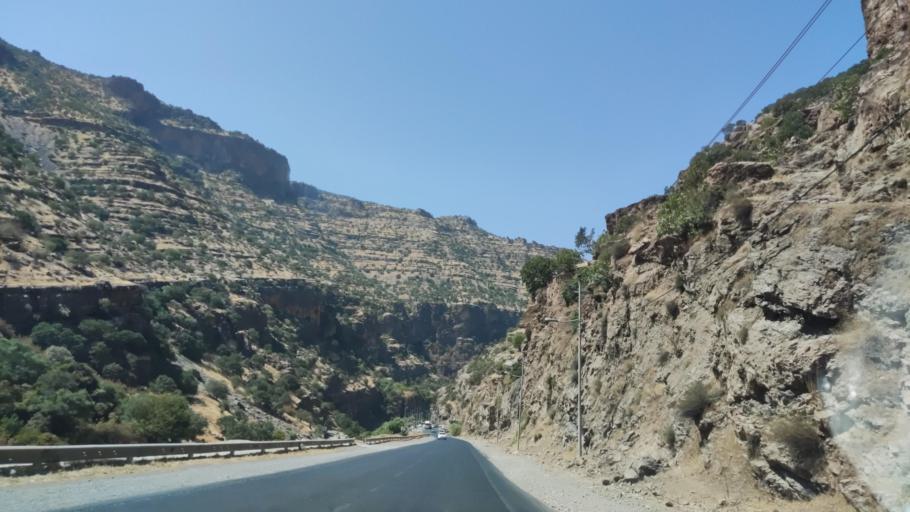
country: IQ
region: Arbil
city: Ruwandiz
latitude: 36.6301
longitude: 44.4733
